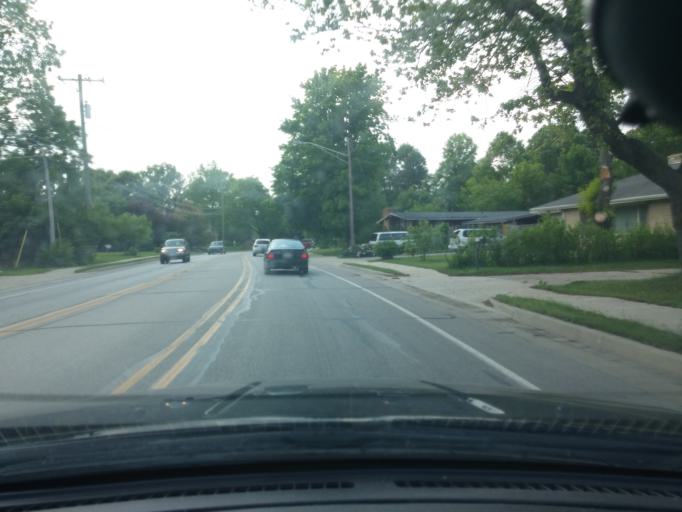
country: US
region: Indiana
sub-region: Tippecanoe County
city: West Lafayette
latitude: 40.4471
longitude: -86.9148
